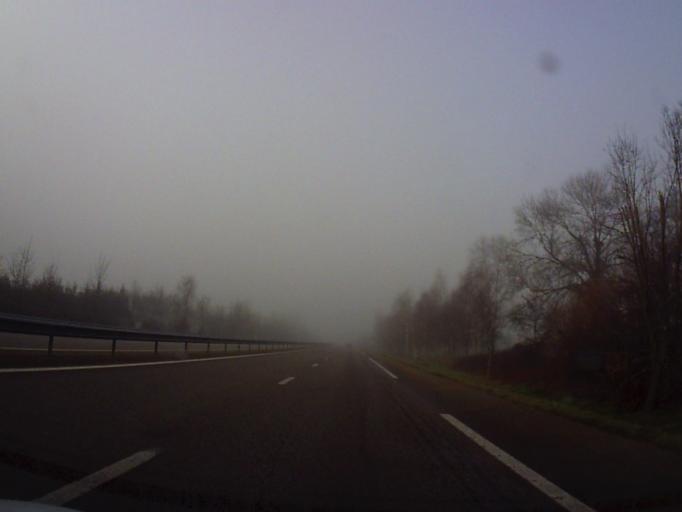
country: FR
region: Brittany
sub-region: Departement du Morbihan
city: Guer
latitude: 47.9419
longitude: -2.1064
